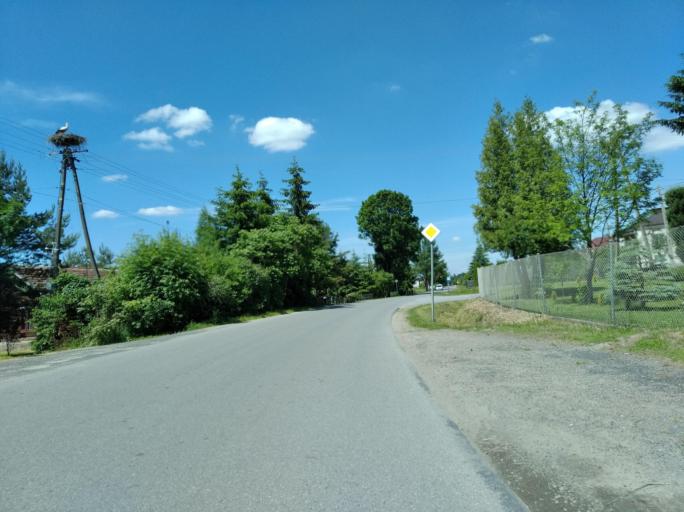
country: PL
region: Subcarpathian Voivodeship
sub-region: Powiat jasielski
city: Nowy Zmigrod
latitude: 49.6183
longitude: 21.5596
